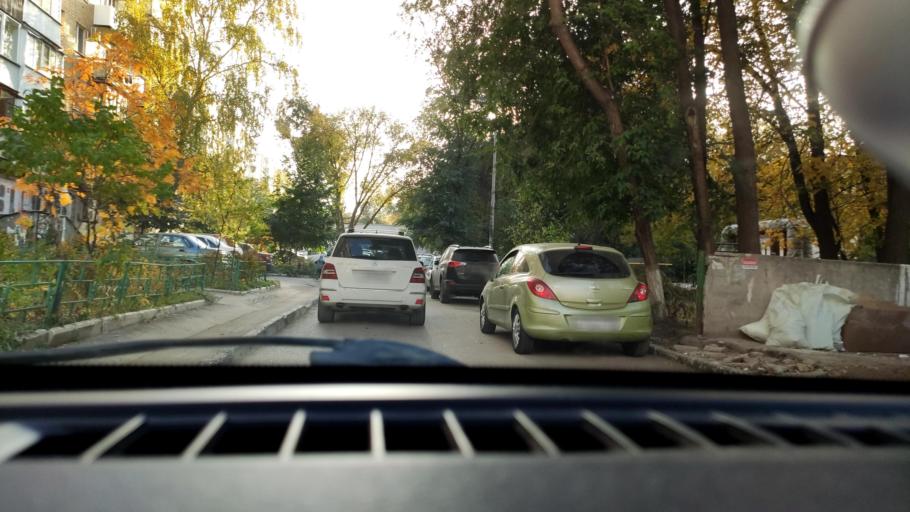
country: RU
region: Samara
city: Samara
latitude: 53.2114
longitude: 50.1362
